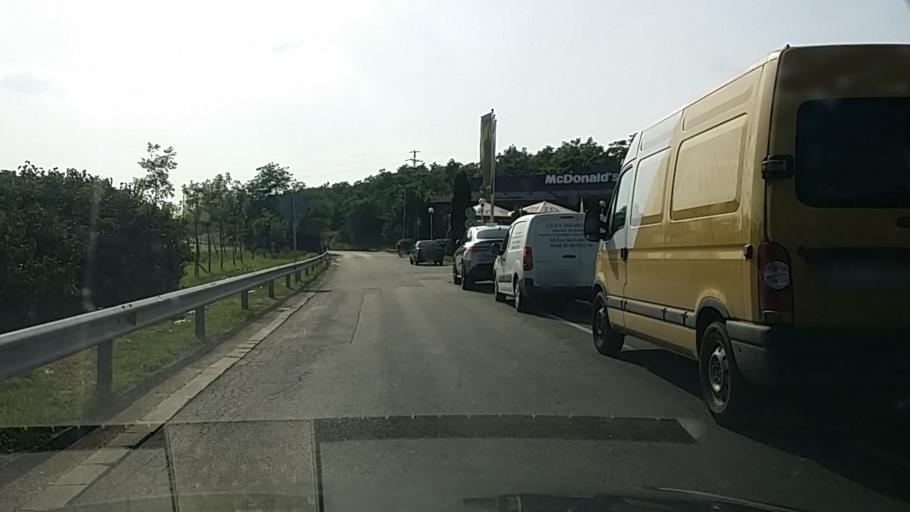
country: HU
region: Pest
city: Toeroekbalint
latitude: 47.4210
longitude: 18.9216
